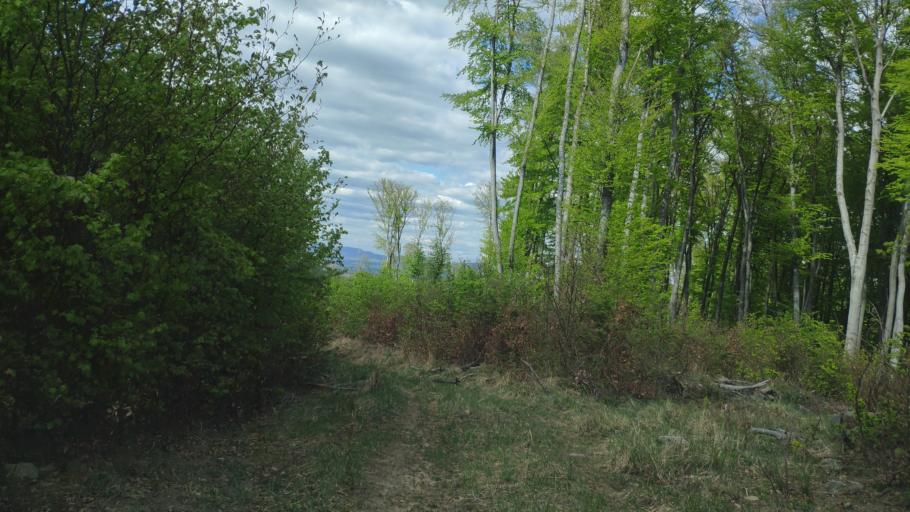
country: SK
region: Kosicky
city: Kosice
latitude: 48.6632
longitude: 21.4506
